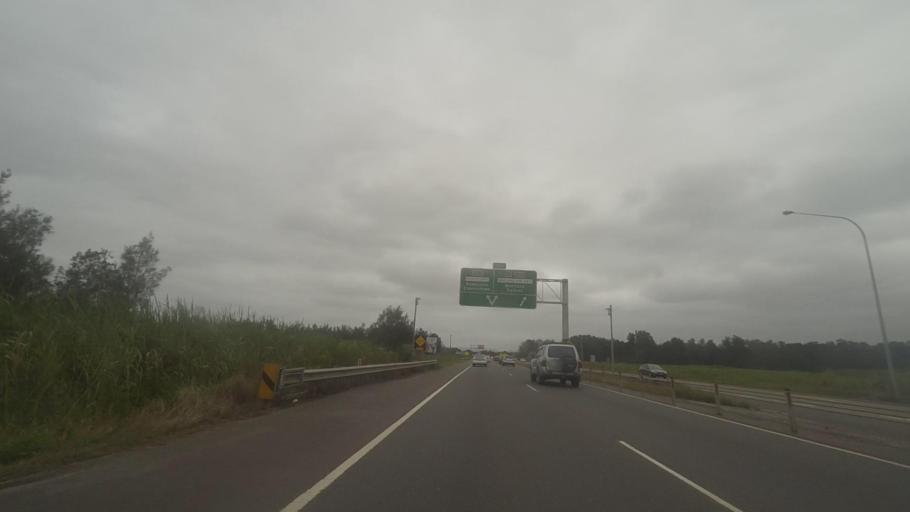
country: AU
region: New South Wales
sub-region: Newcastle
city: Beresfield
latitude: -32.8176
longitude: 151.6943
